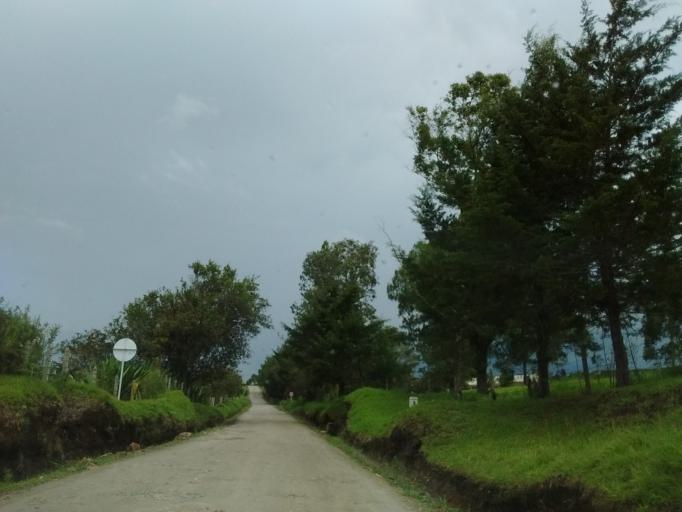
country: CO
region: Cauca
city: Cajibio
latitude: 2.5514
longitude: -76.6265
